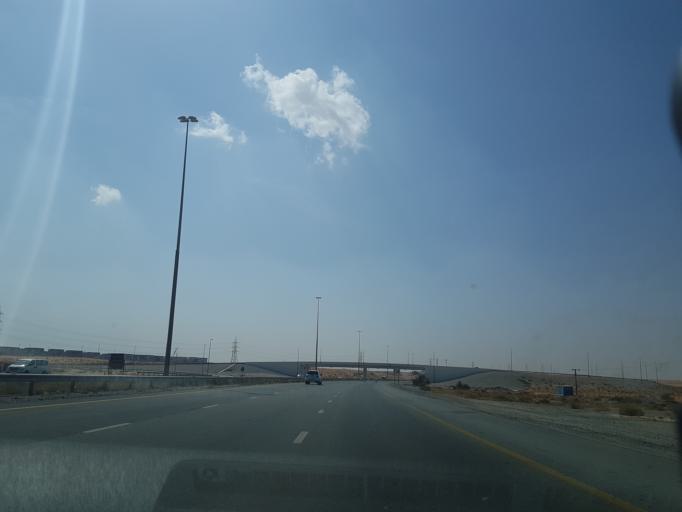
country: AE
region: Ra's al Khaymah
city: Ras al-Khaimah
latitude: 25.6744
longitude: 55.8823
